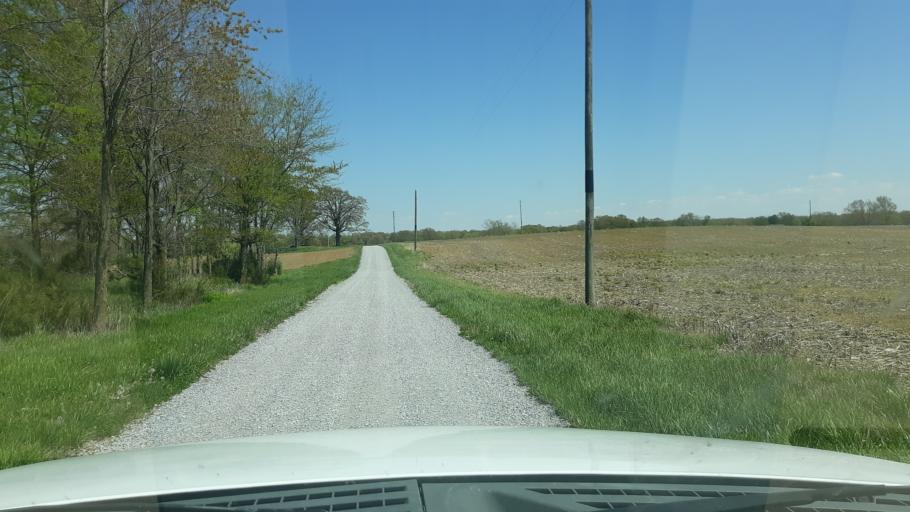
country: US
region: Illinois
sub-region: Saline County
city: Harrisburg
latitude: 37.8849
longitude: -88.6446
